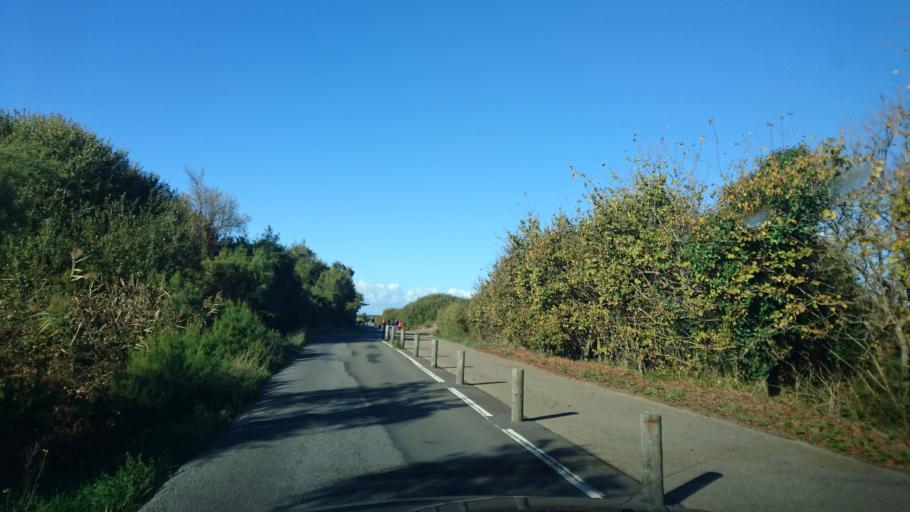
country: FR
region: Pays de la Loire
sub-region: Departement de la Vendee
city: Les Sables-d'Olonne
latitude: 46.5029
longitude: -1.8111
